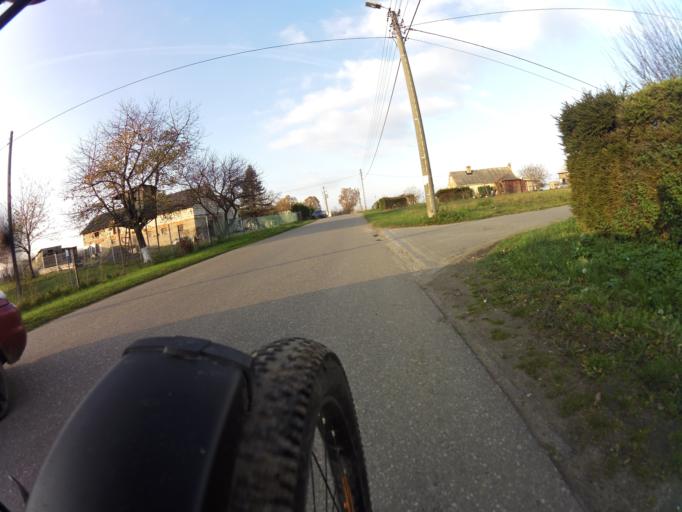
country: PL
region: Pomeranian Voivodeship
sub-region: Powiat pucki
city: Krokowa
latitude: 54.7654
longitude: 18.1809
